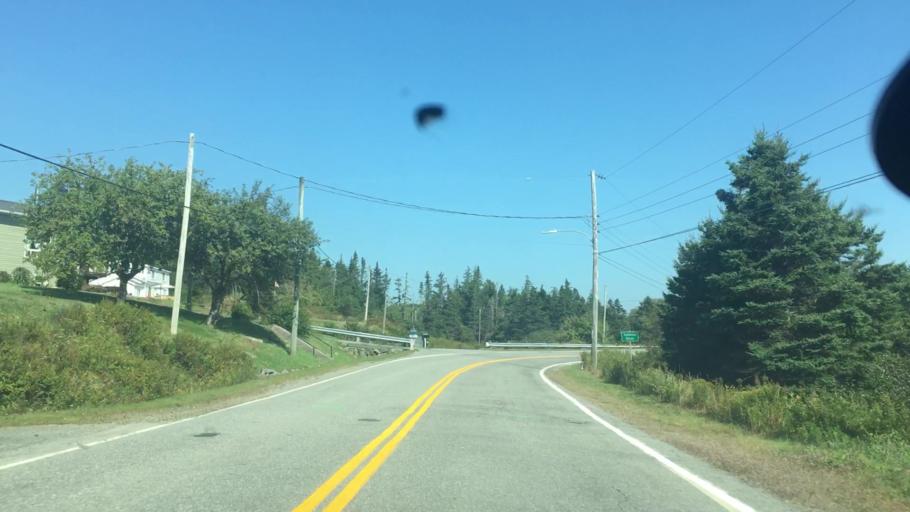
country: CA
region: Nova Scotia
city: New Glasgow
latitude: 44.9155
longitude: -62.3846
